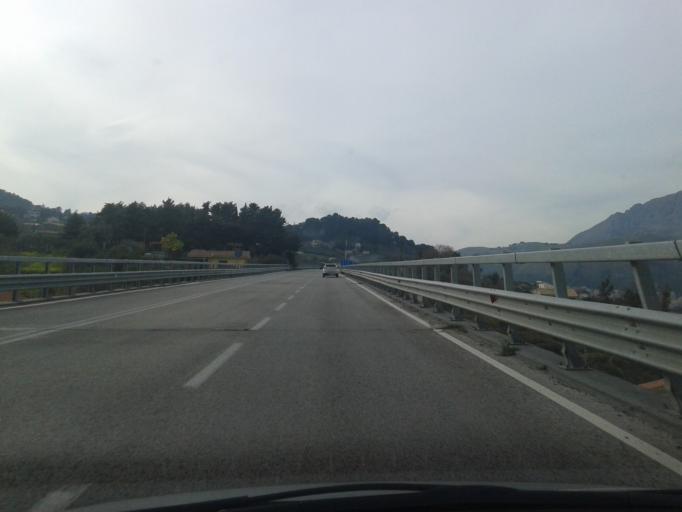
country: IT
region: Sicily
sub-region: Palermo
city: Giacalone
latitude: 38.0347
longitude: 13.2477
